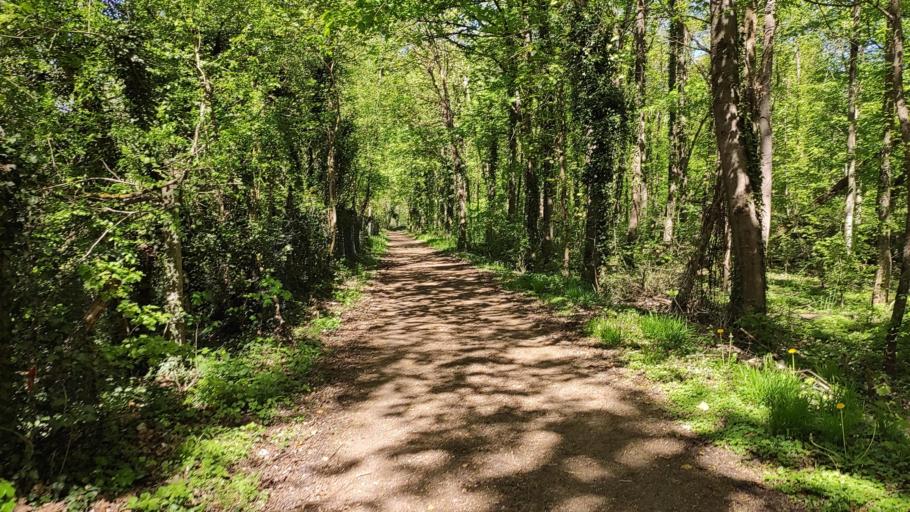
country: DE
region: Baden-Wuerttemberg
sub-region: Freiburg Region
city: Merdingen
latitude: 47.9960
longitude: 7.6598
